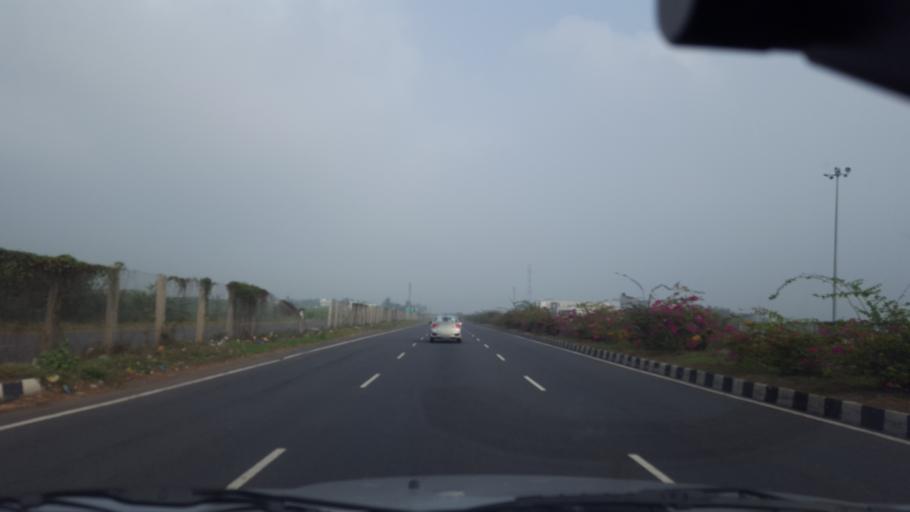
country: IN
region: Andhra Pradesh
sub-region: Prakasam
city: Ongole
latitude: 15.5557
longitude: 80.0541
